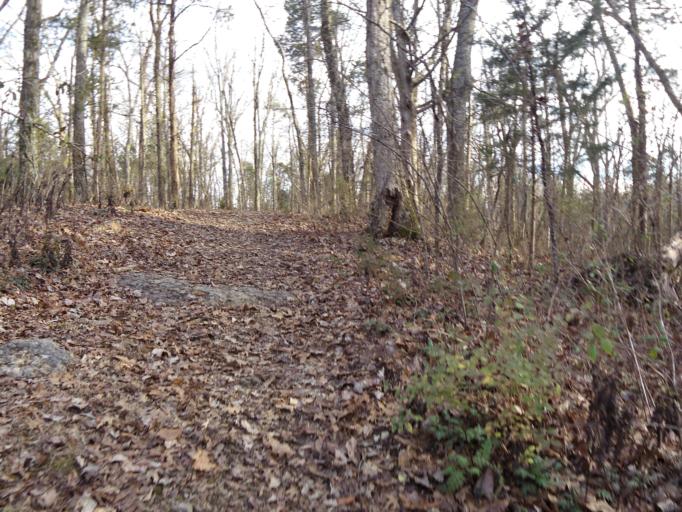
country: US
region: Tennessee
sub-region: Knox County
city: Knoxville
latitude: 35.9508
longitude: -83.8481
